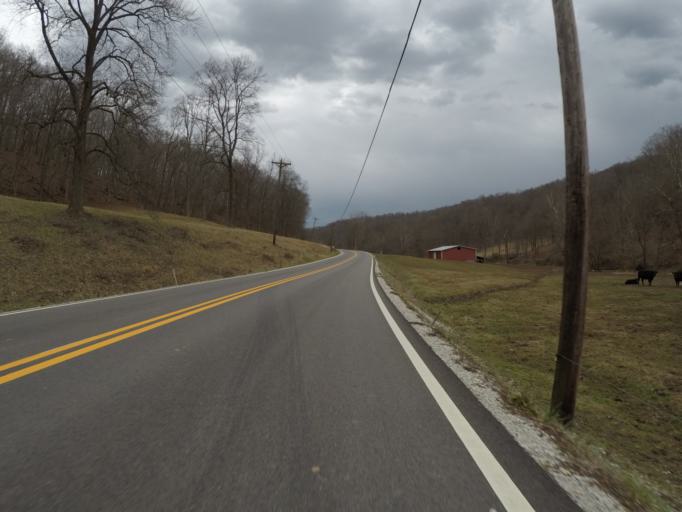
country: US
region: Ohio
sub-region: Lawrence County
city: Burlington
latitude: 38.4540
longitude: -82.5204
